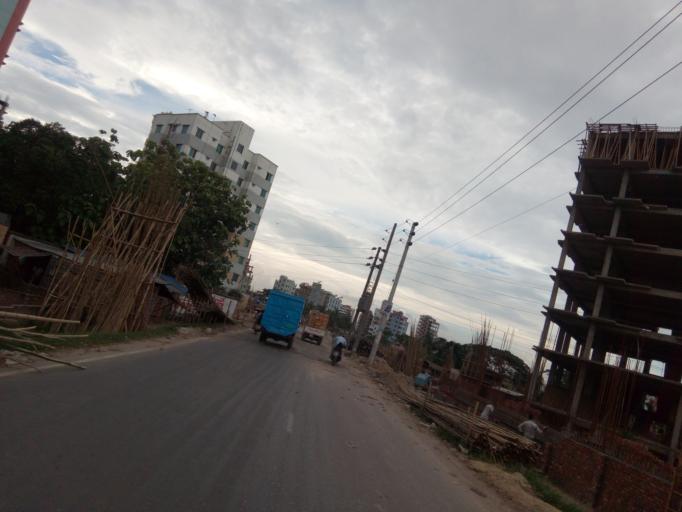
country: BD
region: Dhaka
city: Paltan
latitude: 23.7611
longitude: 90.4452
